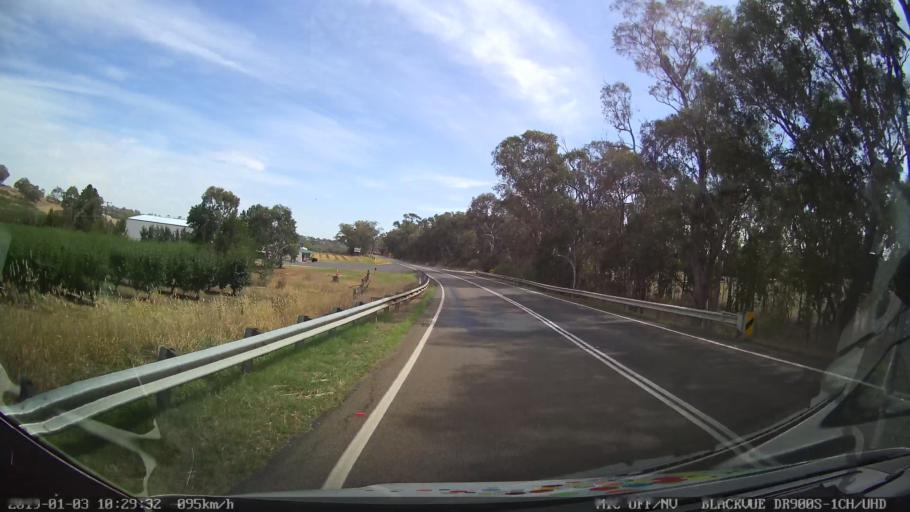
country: AU
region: New South Wales
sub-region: Young
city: Young
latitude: -34.3730
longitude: 148.2614
